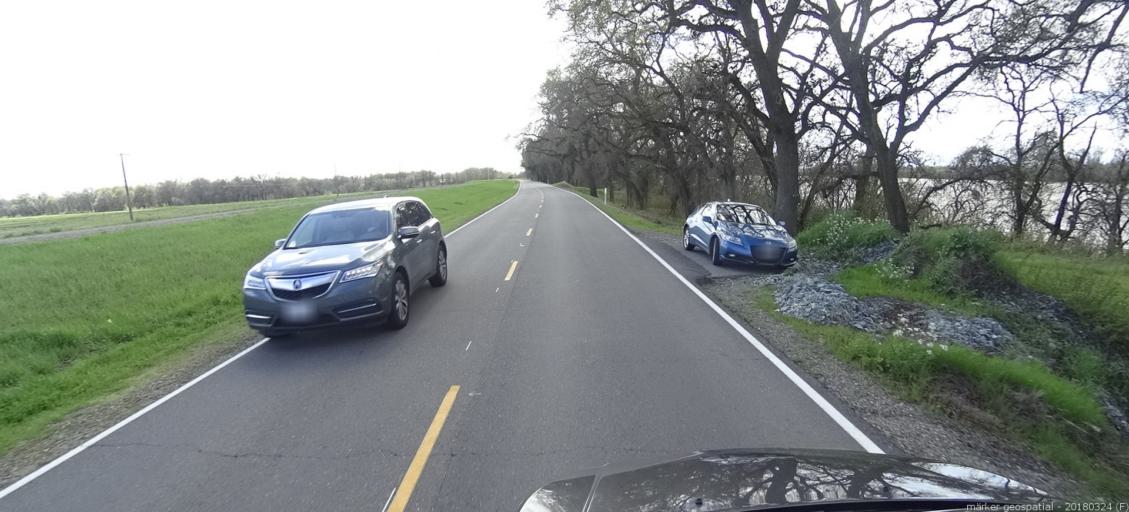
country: US
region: California
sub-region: Sacramento County
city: Elverta
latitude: 38.7082
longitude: -121.6145
